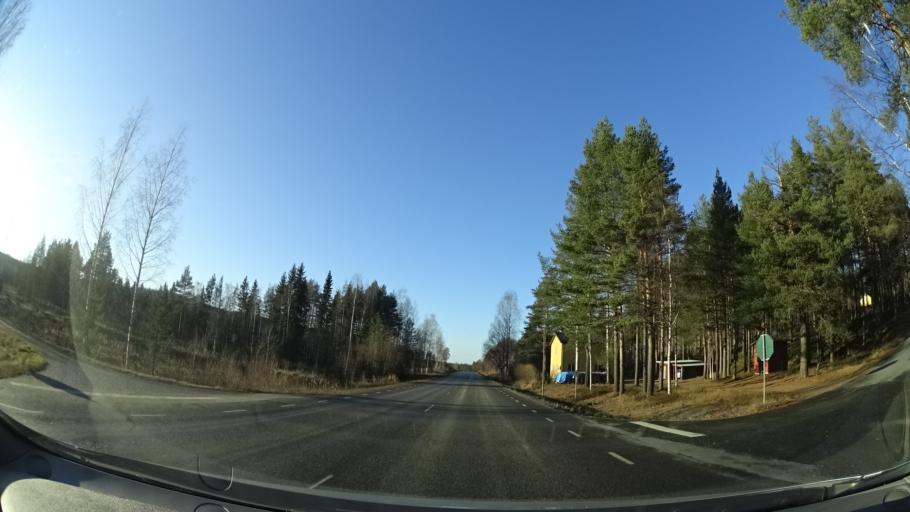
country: SE
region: Vaesterbotten
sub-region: Skelleftea Kommun
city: Langsele
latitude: 64.9174
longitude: 20.0957
